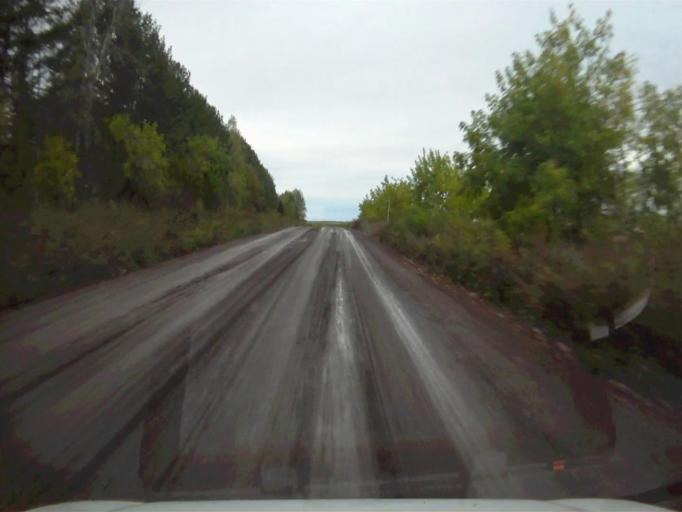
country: RU
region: Sverdlovsk
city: Mikhaylovsk
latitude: 56.1563
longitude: 59.2583
